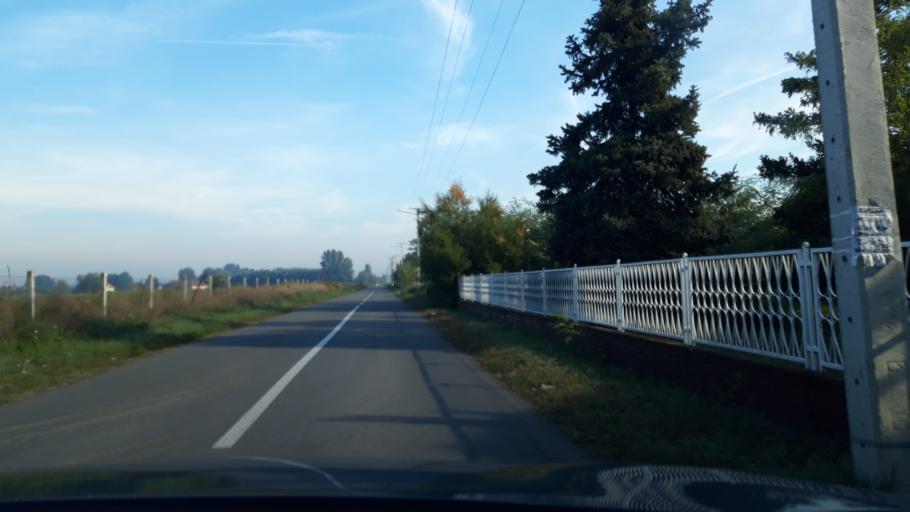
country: HU
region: Csongrad
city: Asotthalom
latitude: 46.1187
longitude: 19.8441
